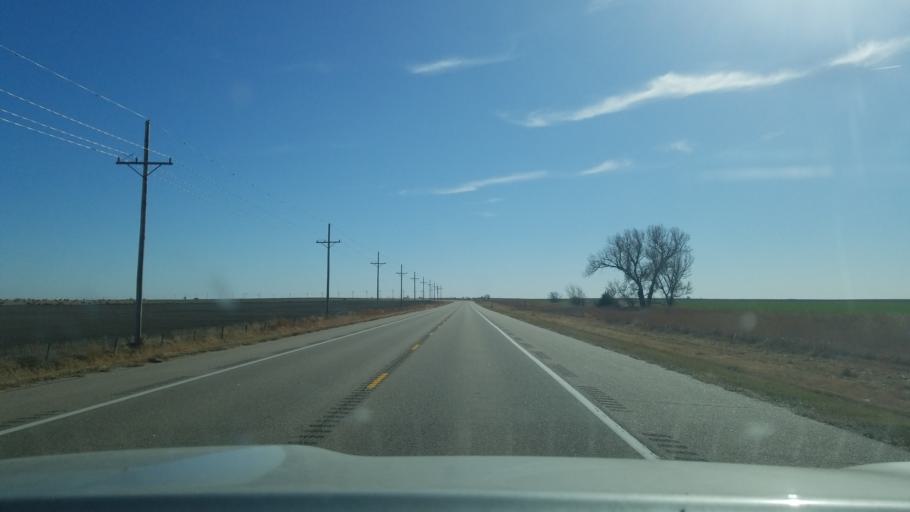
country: US
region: Kansas
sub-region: Ford County
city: Dodge City
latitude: 37.5928
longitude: -99.6913
